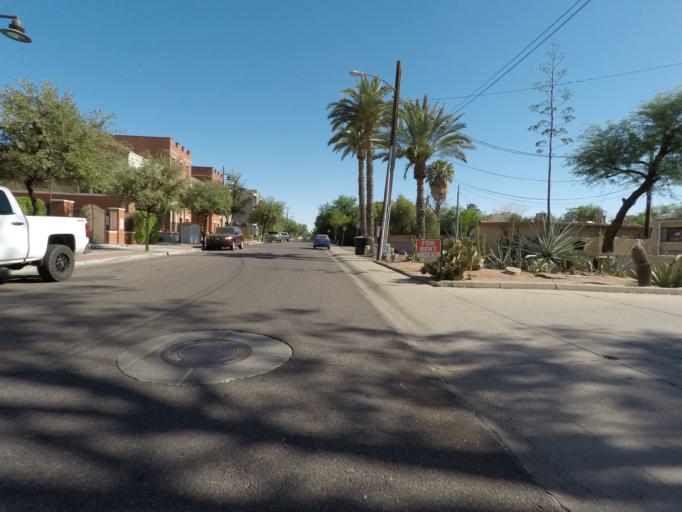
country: US
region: Arizona
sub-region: Maricopa County
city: Tempe Junction
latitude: 33.4241
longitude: -111.9473
